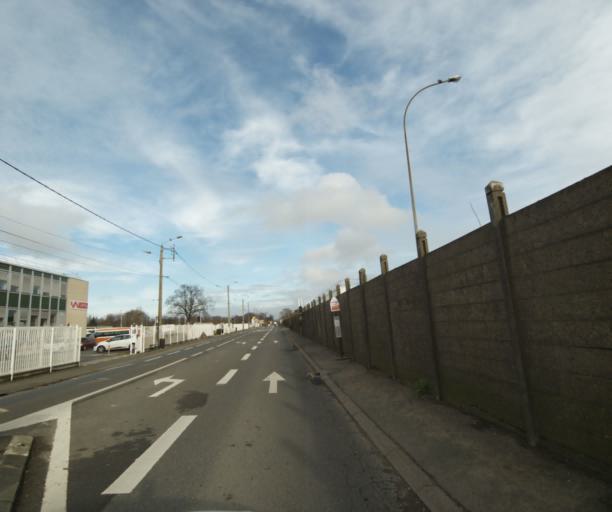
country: FR
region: Pays de la Loire
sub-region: Departement de la Sarthe
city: Allonnes
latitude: 47.9766
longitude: 0.1761
